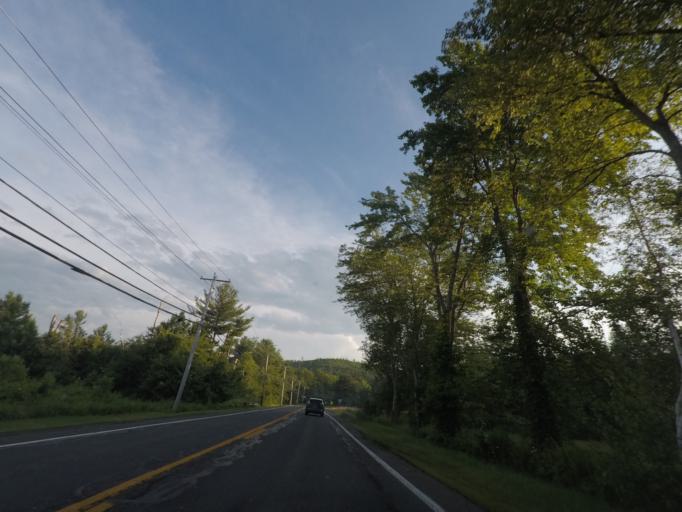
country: US
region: Massachusetts
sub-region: Hampden County
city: Brimfield
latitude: 42.1166
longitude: -72.2243
